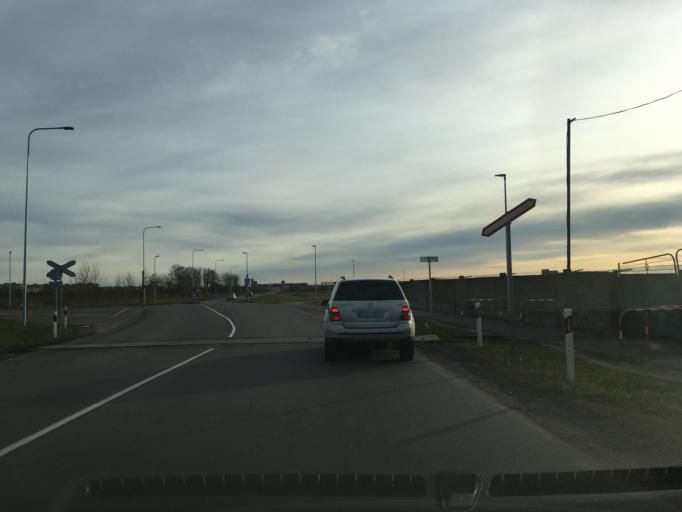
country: EE
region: Ida-Virumaa
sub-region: Narva linn
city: Narva
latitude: 59.3682
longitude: 28.1581
